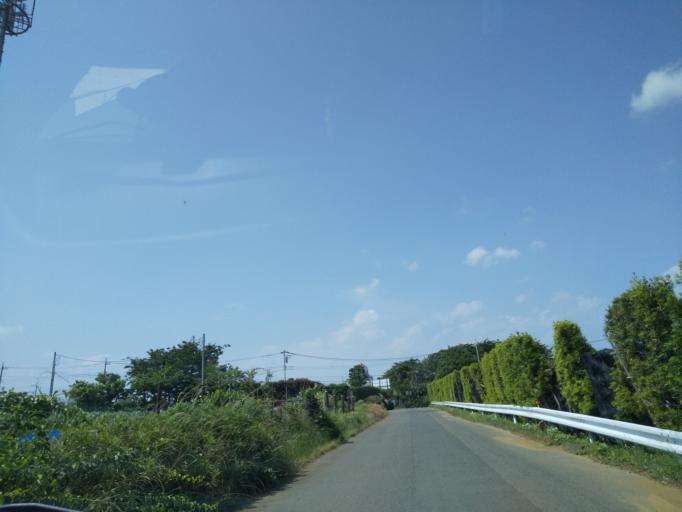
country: JP
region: Kanagawa
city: Zama
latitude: 35.5181
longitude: 139.3900
